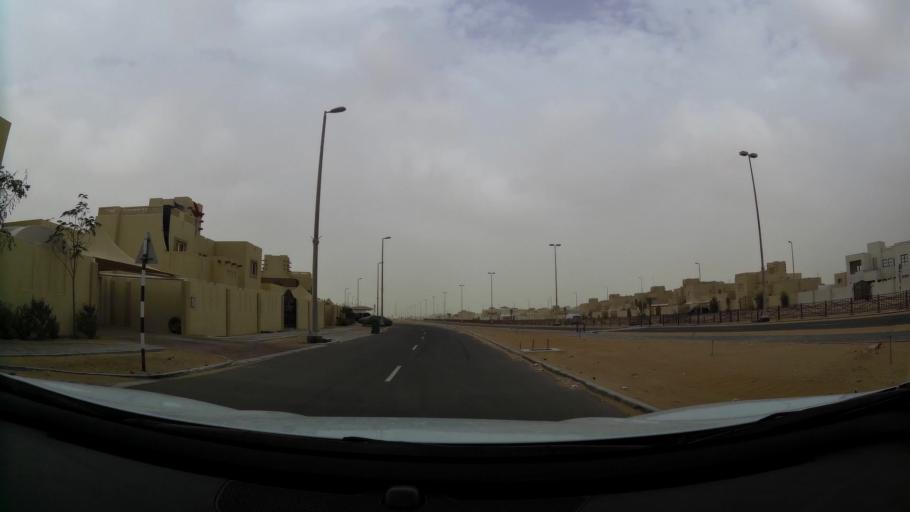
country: AE
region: Abu Dhabi
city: Abu Dhabi
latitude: 24.4508
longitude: 54.7188
